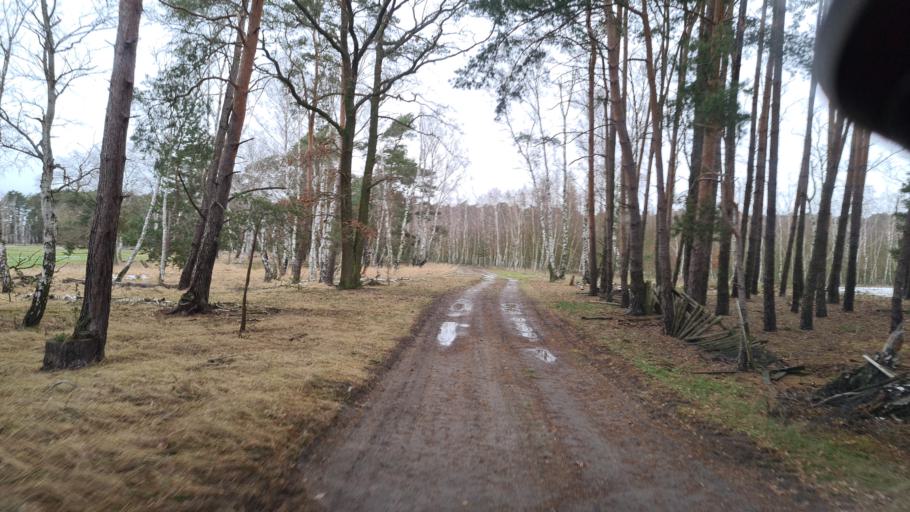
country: DE
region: Brandenburg
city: Schenkendobern
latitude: 51.9091
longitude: 14.5920
